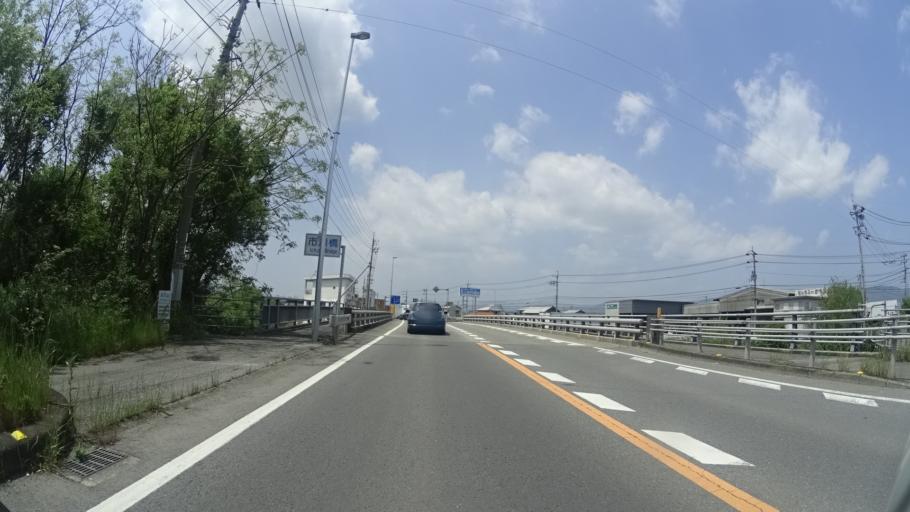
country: JP
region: Tokushima
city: Kamojimacho-jogejima
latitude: 34.0735
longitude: 134.3928
